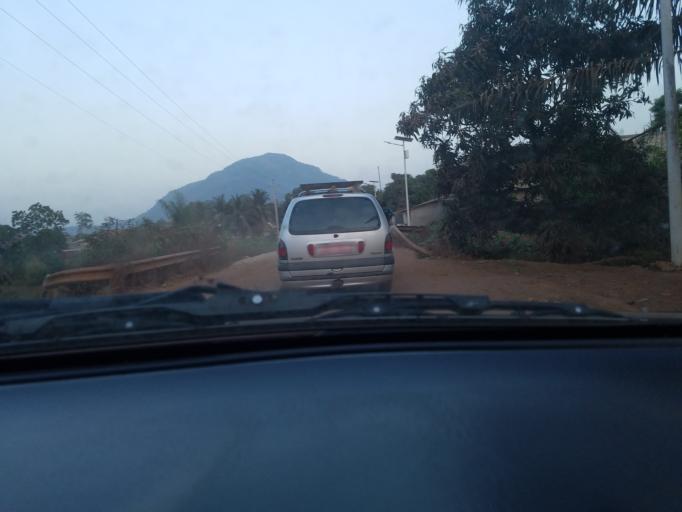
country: GN
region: Kindia
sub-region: Prefecture de Dubreka
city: Dubreka
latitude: 9.7887
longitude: -13.5011
